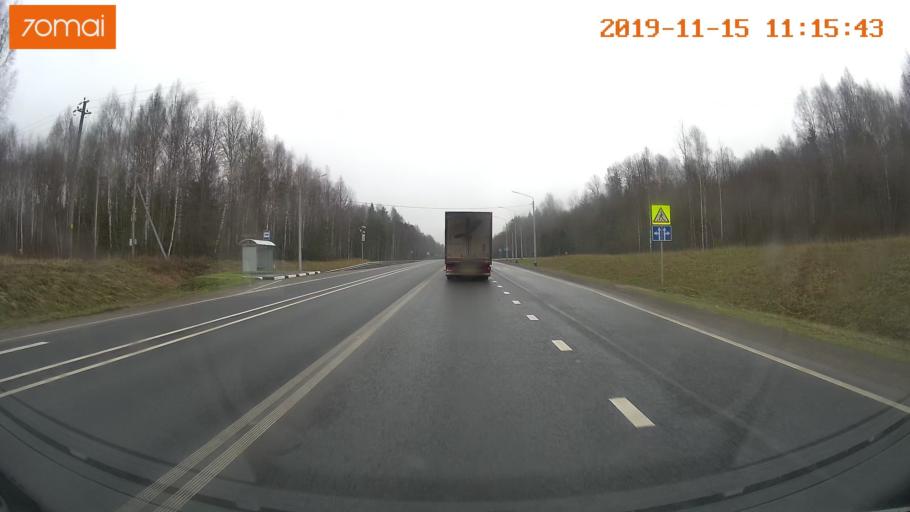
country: RU
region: Vologda
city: Chebsara
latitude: 59.1283
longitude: 39.2148
